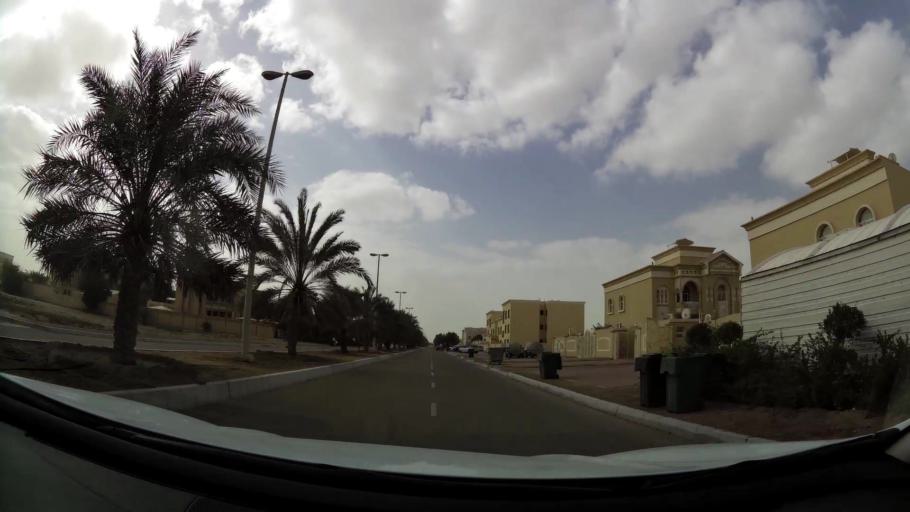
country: AE
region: Abu Dhabi
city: Abu Dhabi
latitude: 24.4124
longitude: 54.4972
